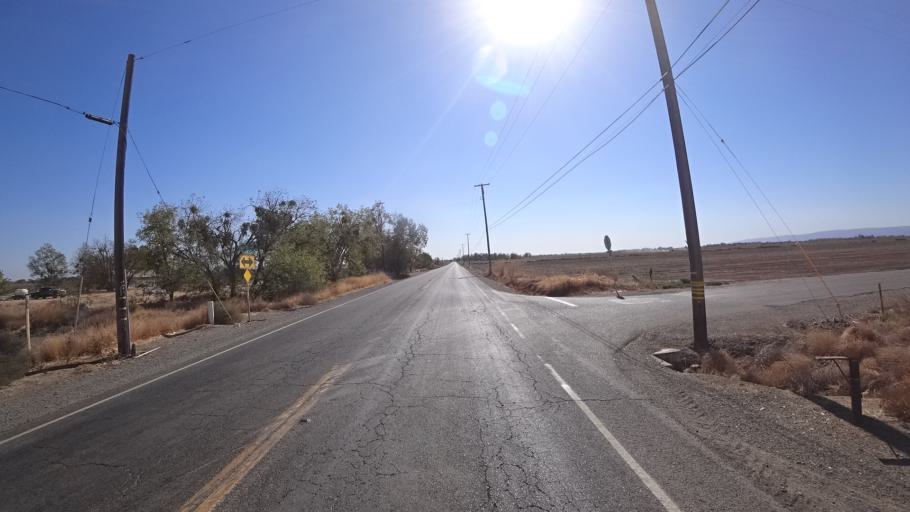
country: US
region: California
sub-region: Yolo County
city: Davis
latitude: 38.5762
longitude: -121.8033
